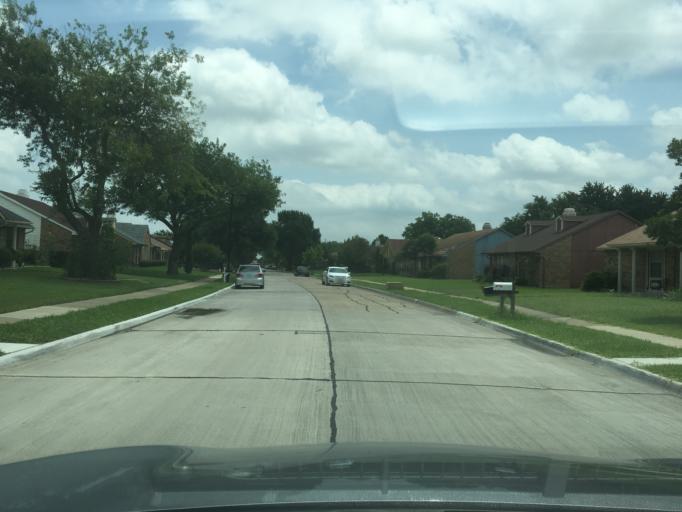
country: US
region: Texas
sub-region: Dallas County
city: Garland
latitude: 32.9201
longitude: -96.6708
